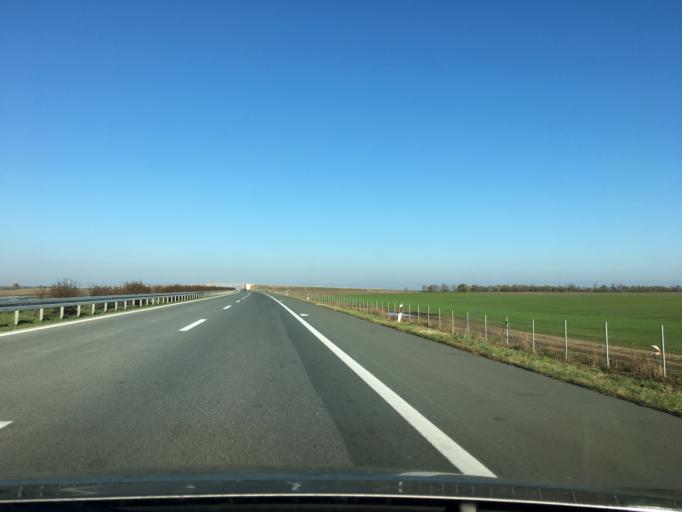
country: RS
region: Autonomna Pokrajina Vojvodina
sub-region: Severnobacki Okrug
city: Mali Igos
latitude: 45.6907
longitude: 19.7256
